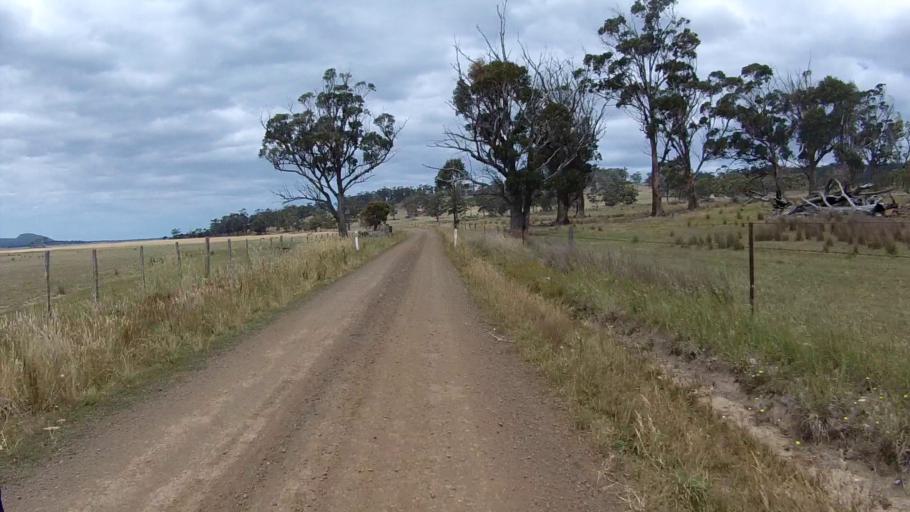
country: AU
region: Tasmania
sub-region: Sorell
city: Sorell
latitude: -42.6595
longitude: 147.9415
